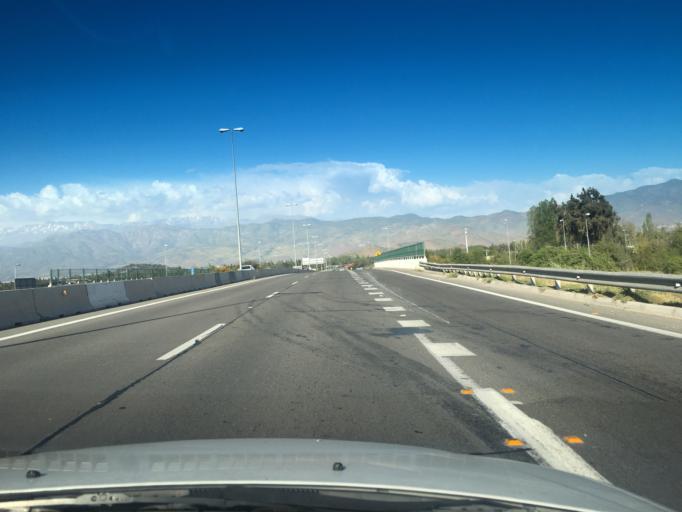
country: CL
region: Santiago Metropolitan
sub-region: Provincia de Chacabuco
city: Chicureo Abajo
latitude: -33.2914
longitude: -70.7026
